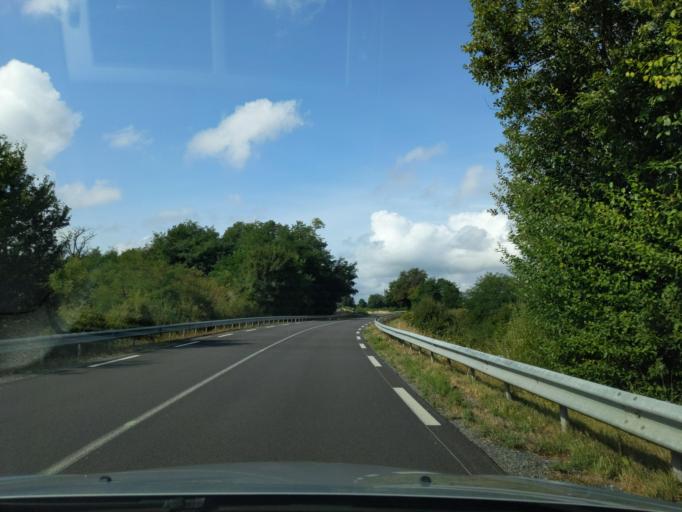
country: FR
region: Bourgogne
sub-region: Departement de la Nievre
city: Luzy
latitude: 46.8426
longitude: 4.0555
